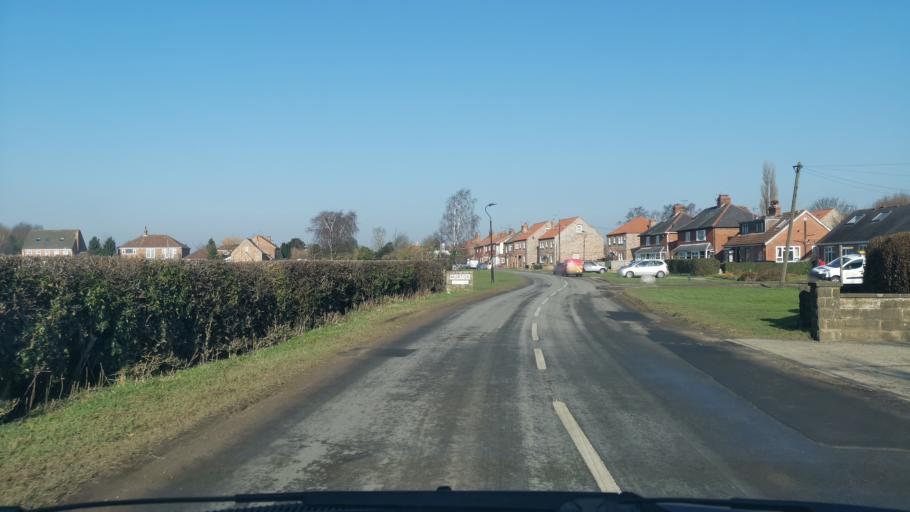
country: GB
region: England
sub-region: City of York
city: Murton
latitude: 53.9648
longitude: -1.0101
